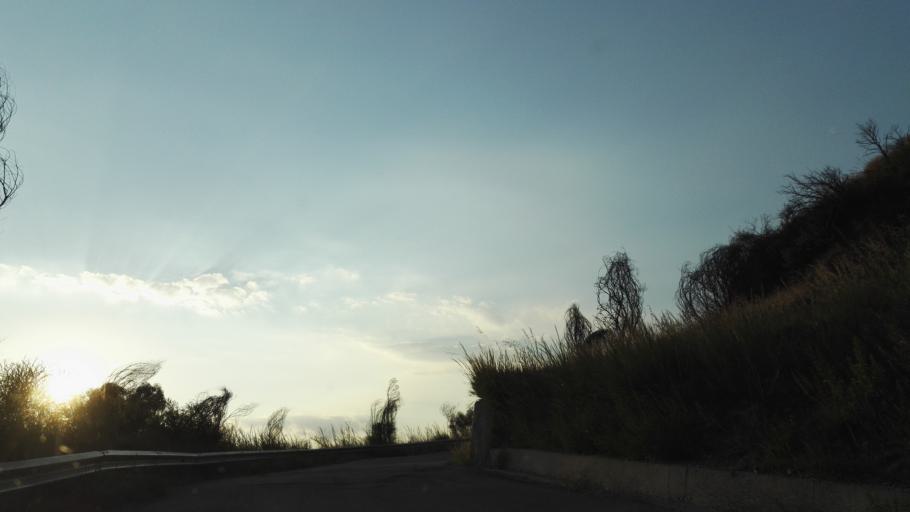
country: IT
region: Calabria
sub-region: Provincia di Reggio Calabria
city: Caulonia
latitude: 38.3986
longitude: 16.4293
